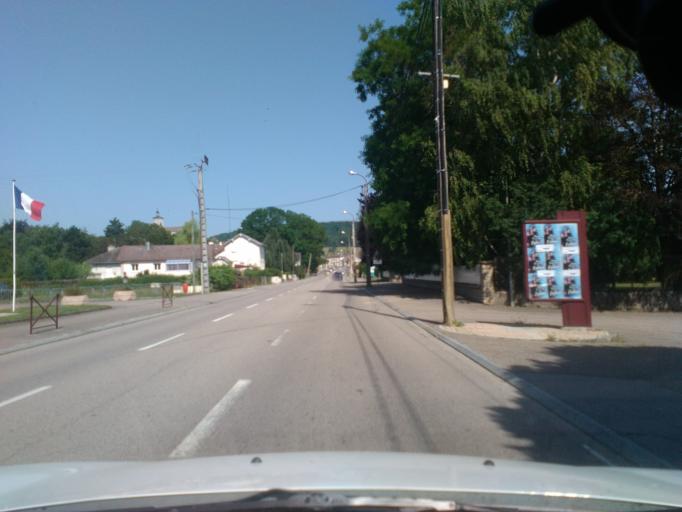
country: FR
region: Lorraine
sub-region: Departement des Vosges
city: Chatenois
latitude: 48.3001
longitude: 5.8405
